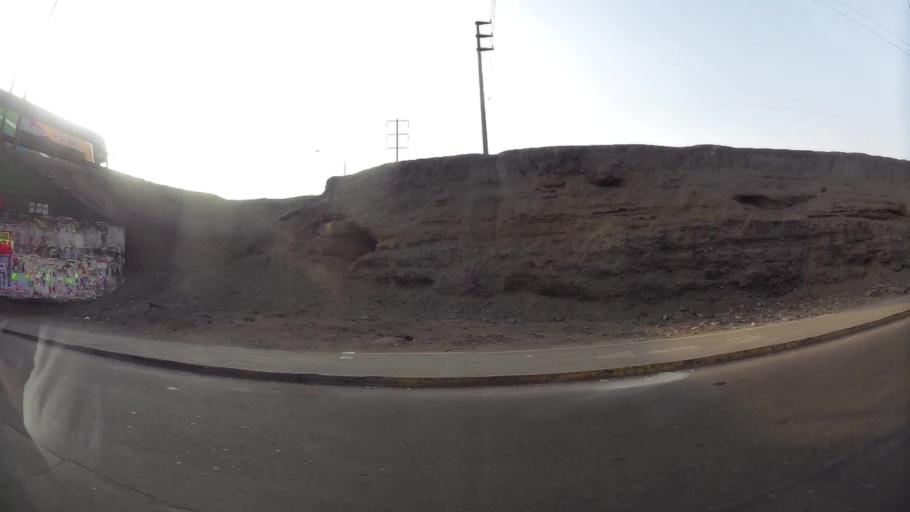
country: PE
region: Lima
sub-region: Lima
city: Independencia
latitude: -11.9624
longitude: -77.0682
